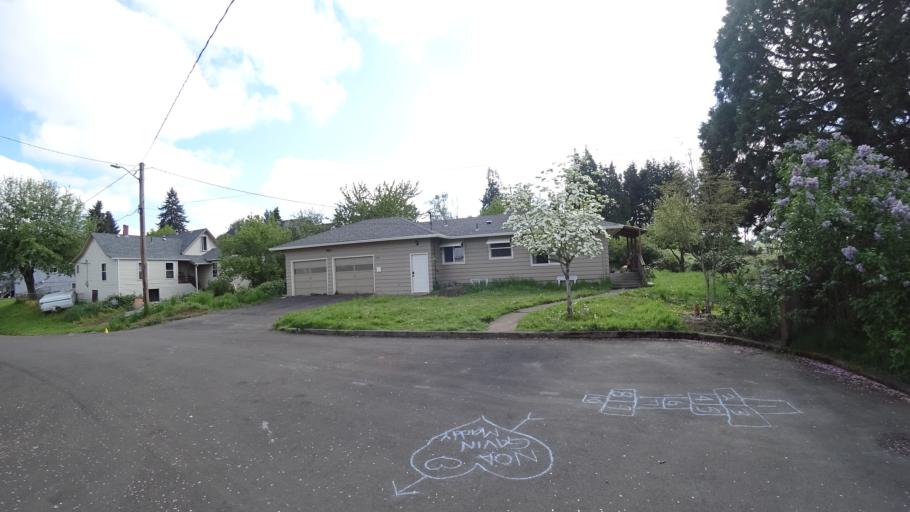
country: US
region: Oregon
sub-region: Washington County
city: Hillsboro
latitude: 45.5145
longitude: -122.9882
